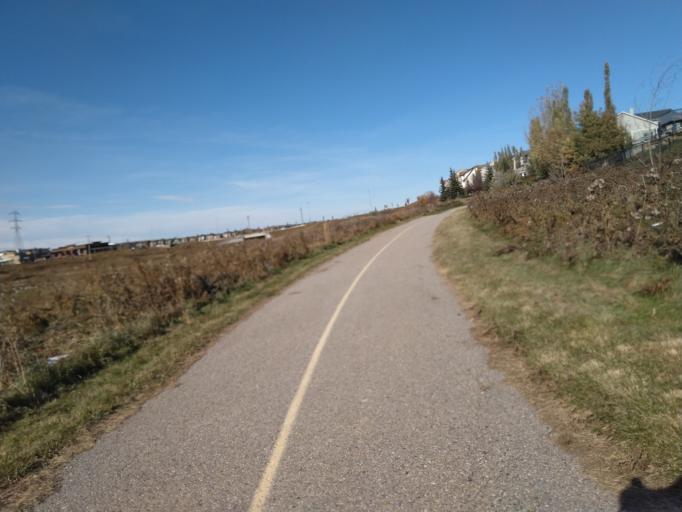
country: CA
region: Alberta
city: Calgary
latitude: 51.1652
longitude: -114.1255
